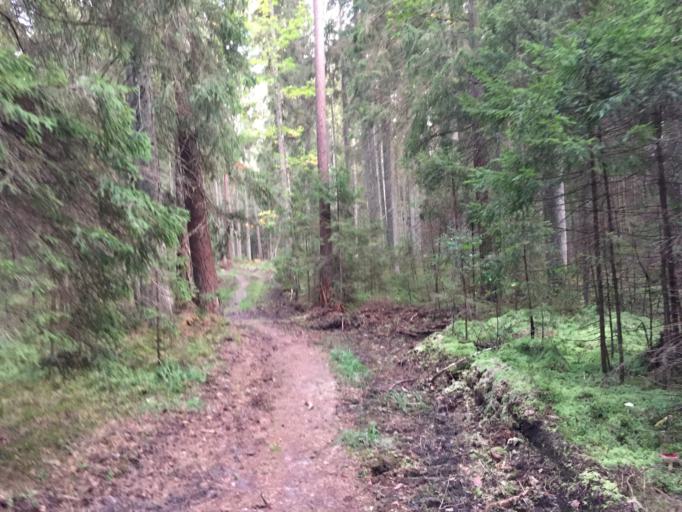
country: LV
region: Baldone
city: Baldone
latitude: 56.7561
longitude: 24.4040
